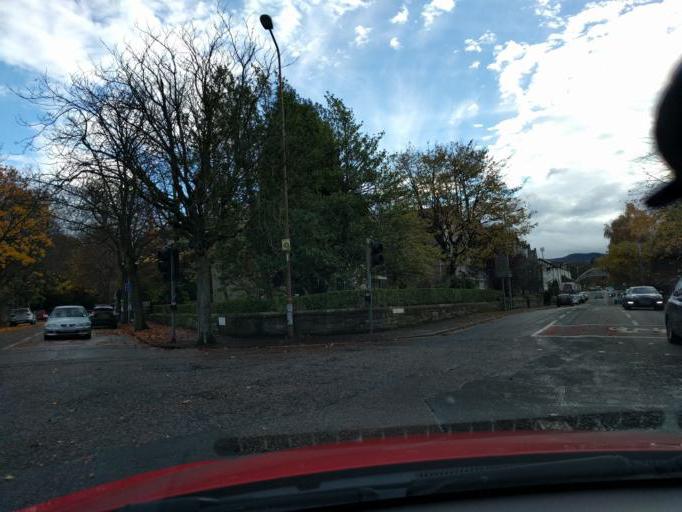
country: GB
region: Scotland
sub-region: Edinburgh
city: Edinburgh
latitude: 55.9298
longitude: -3.2238
